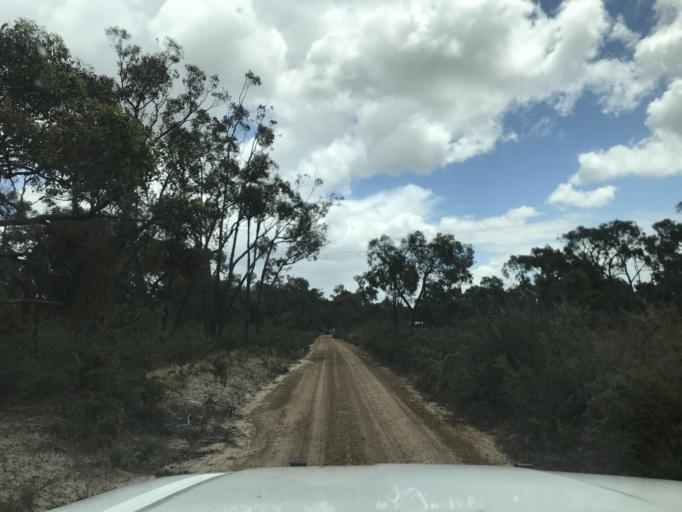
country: AU
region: South Australia
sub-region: Wattle Range
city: Penola
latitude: -37.0891
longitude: 141.3362
